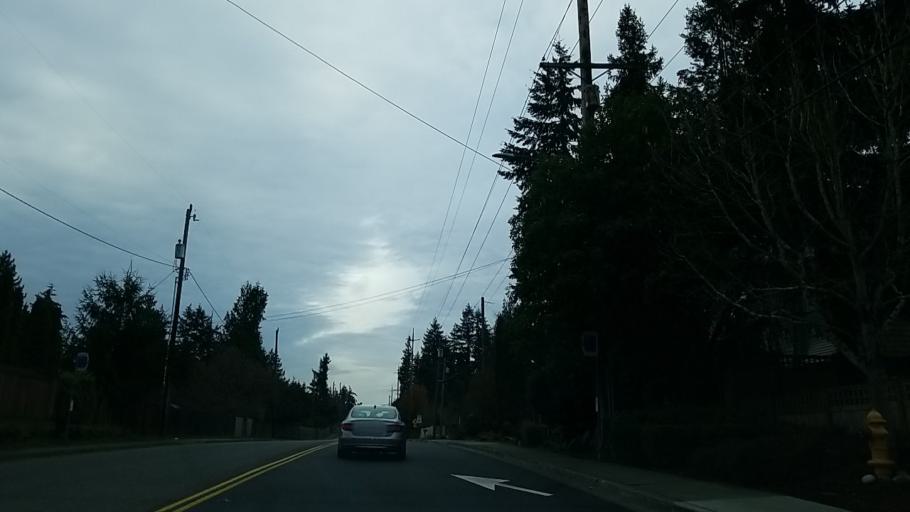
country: US
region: Washington
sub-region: Snohomish County
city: Esperance
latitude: 47.7778
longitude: -122.3483
